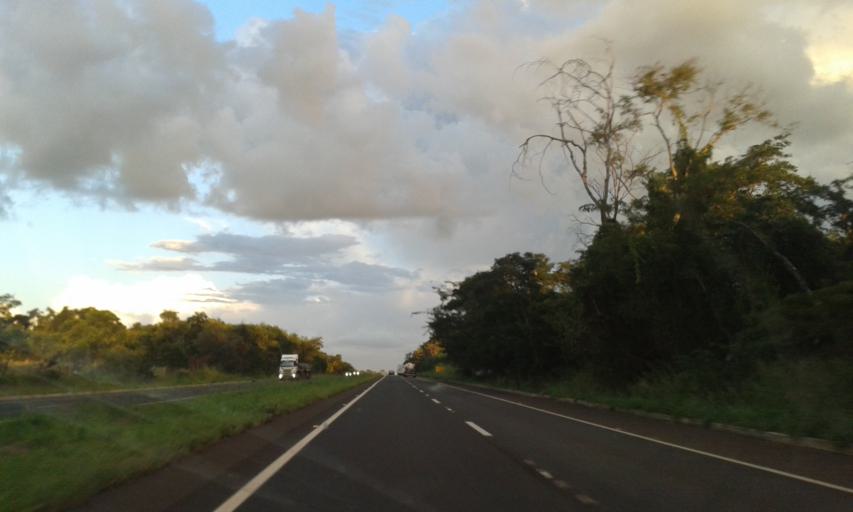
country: BR
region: Minas Gerais
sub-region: Monte Alegre De Minas
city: Monte Alegre de Minas
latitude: -18.8613
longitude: -48.7687
